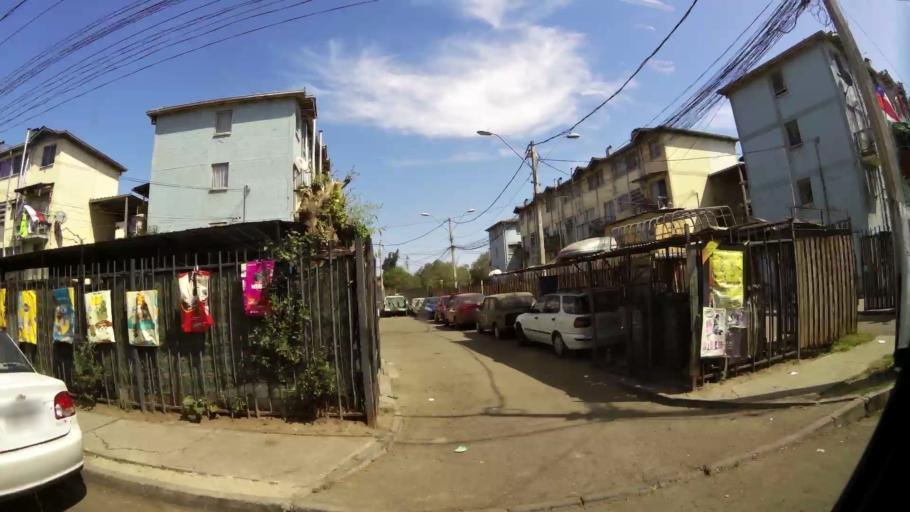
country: CL
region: Santiago Metropolitan
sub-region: Provincia de Santiago
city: Lo Prado
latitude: -33.4809
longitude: -70.7208
